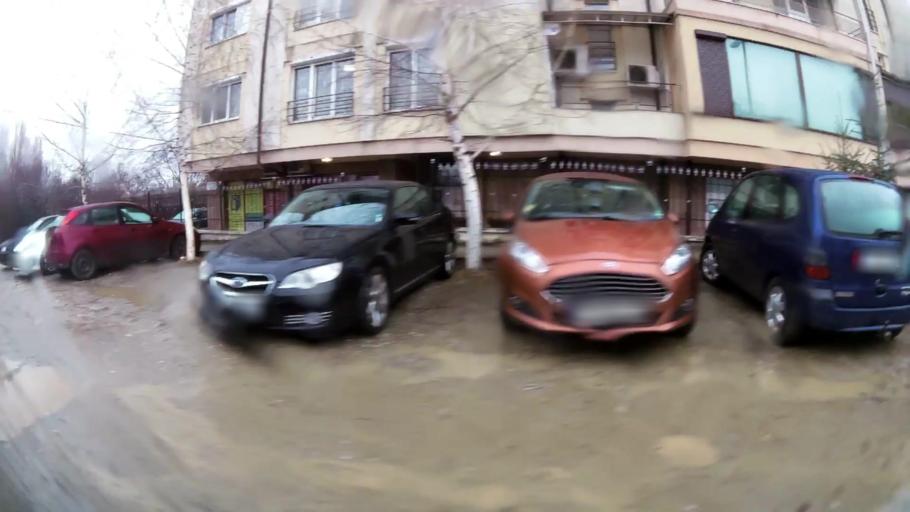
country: BG
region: Sofia-Capital
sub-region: Stolichna Obshtina
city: Sofia
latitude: 42.6515
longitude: 23.3295
